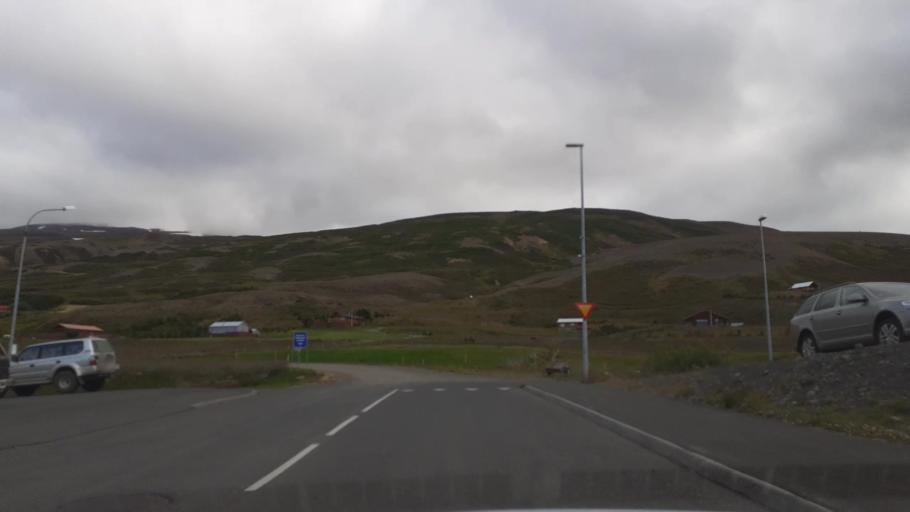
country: IS
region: Northeast
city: Akureyri
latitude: 65.9520
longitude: -18.1782
